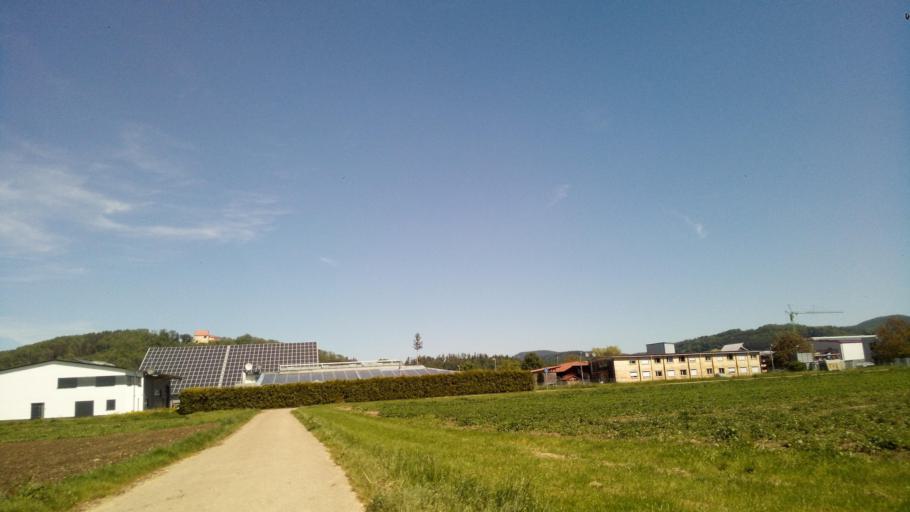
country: DE
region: Baden-Wuerttemberg
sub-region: Regierungsbezirk Stuttgart
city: Donzdorf
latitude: 48.6805
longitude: 9.7909
